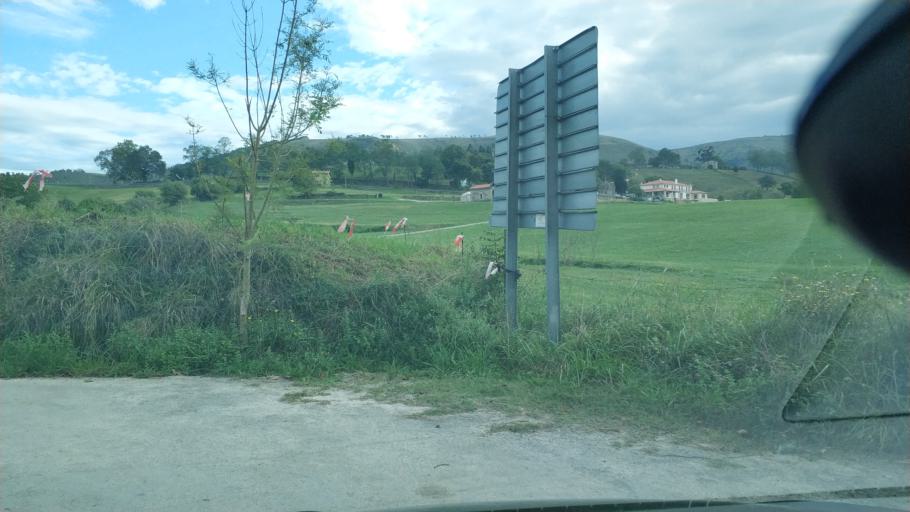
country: ES
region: Cantabria
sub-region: Provincia de Cantabria
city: Santa Maria de Cayon
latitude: 43.2834
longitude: -3.8134
